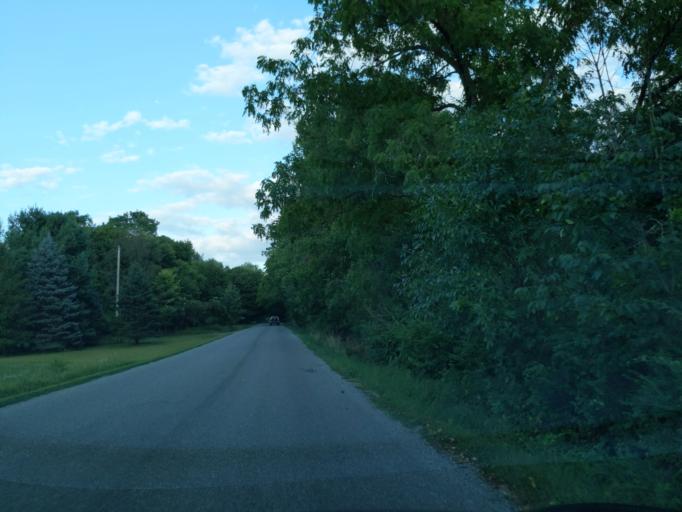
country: US
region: Michigan
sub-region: Eaton County
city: Dimondale
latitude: 42.5969
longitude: -84.5880
